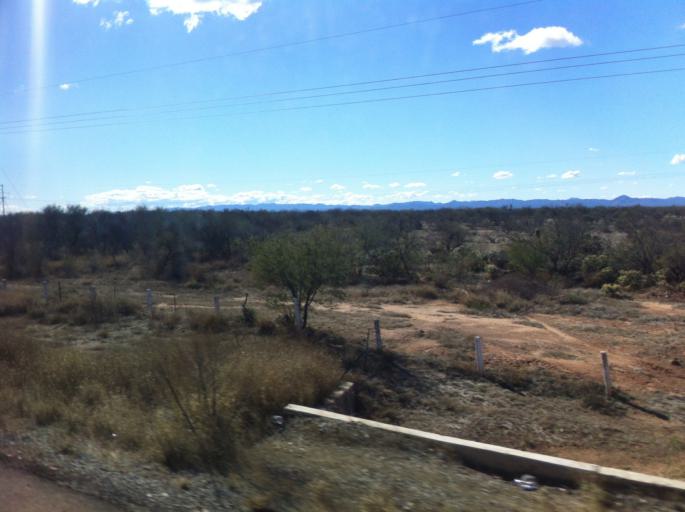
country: MX
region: Sonora
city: Benjamin Hill
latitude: 30.3379
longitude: -111.0985
